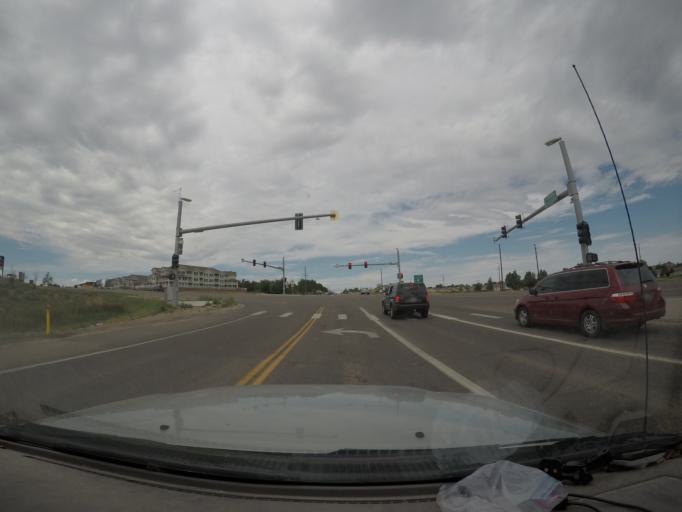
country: US
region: Wyoming
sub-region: Laramie County
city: Fox Farm-College
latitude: 41.1455
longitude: -104.7555
